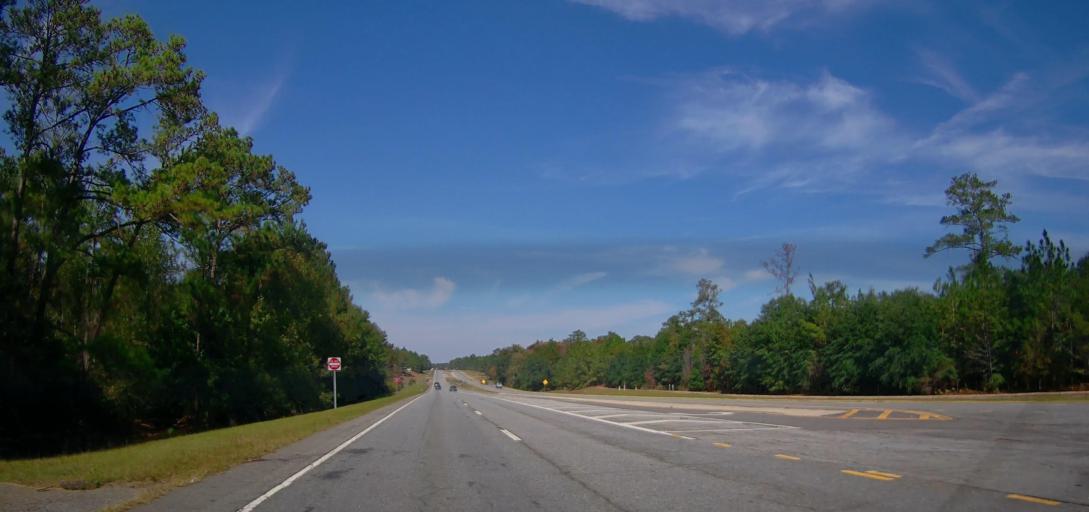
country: US
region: Georgia
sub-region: Lee County
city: Leesburg
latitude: 31.7151
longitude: -83.9891
